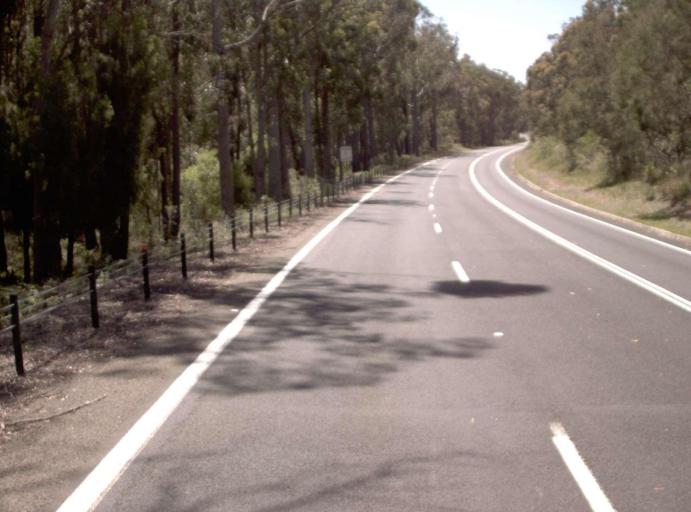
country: AU
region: Victoria
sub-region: East Gippsland
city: Lakes Entrance
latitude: -37.7927
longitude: 148.0496
